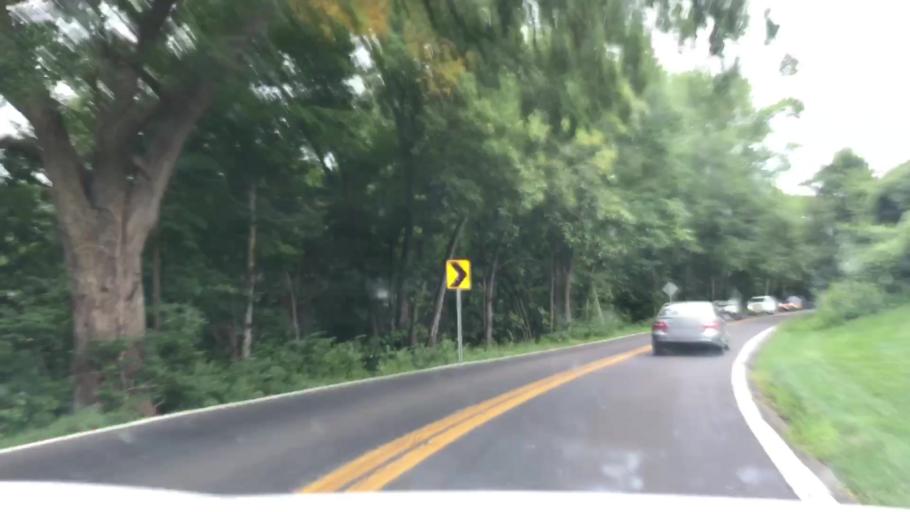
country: US
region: Missouri
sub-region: Saint Louis County
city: Chesterfield
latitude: 38.6524
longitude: -90.6153
